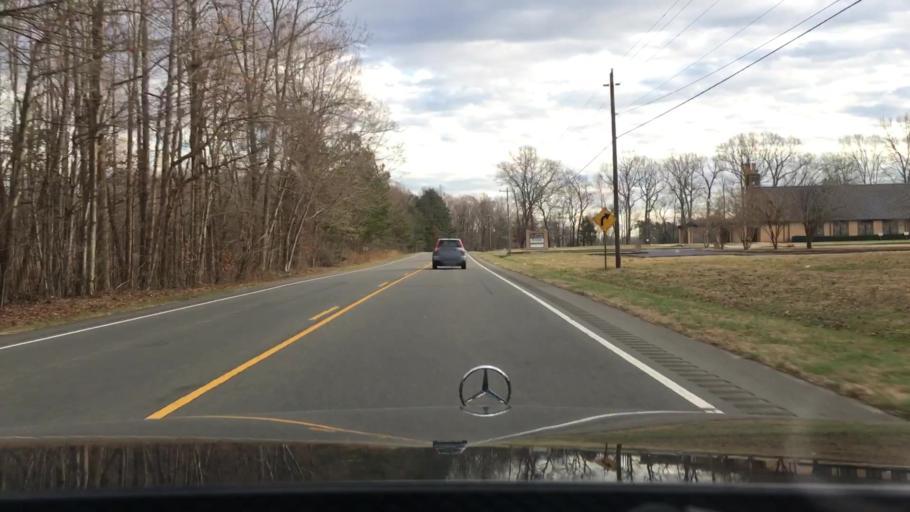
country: US
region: North Carolina
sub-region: Orange County
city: Hillsborough
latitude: 36.1710
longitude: -79.1323
